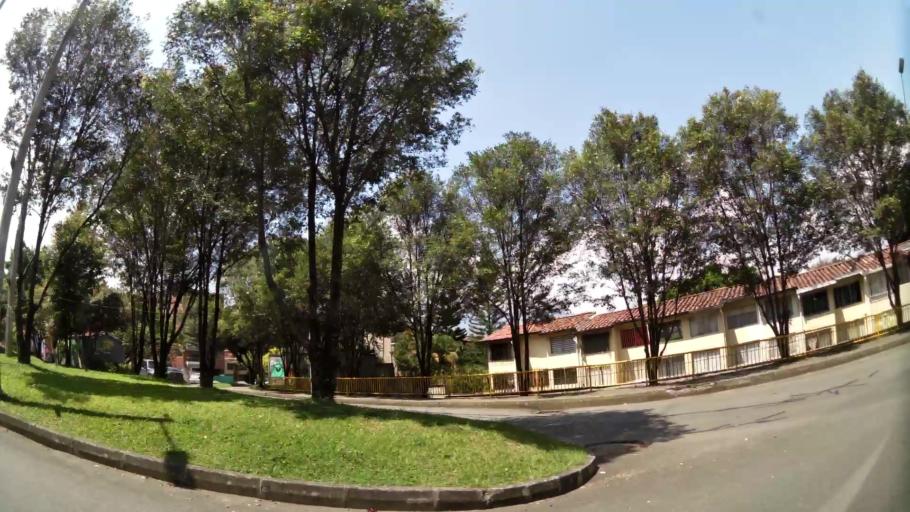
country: CO
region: Antioquia
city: Itagui
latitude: 6.2211
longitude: -75.6054
